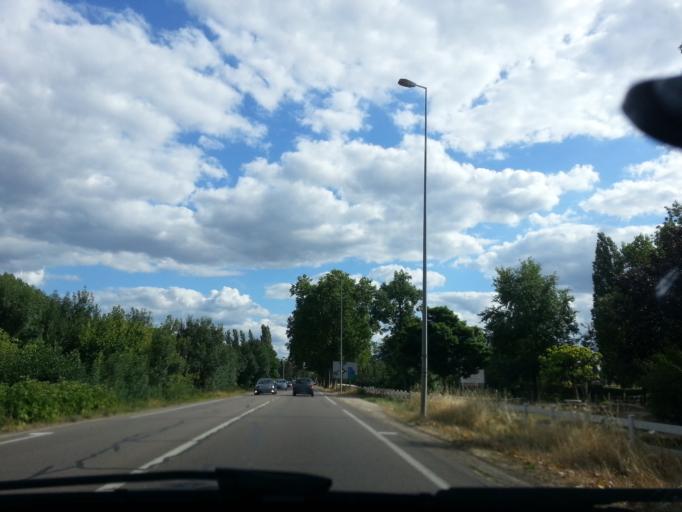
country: FR
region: Bourgogne
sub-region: Departement de Saone-et-Loire
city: Saint-Remy
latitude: 46.7623
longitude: 4.8426
